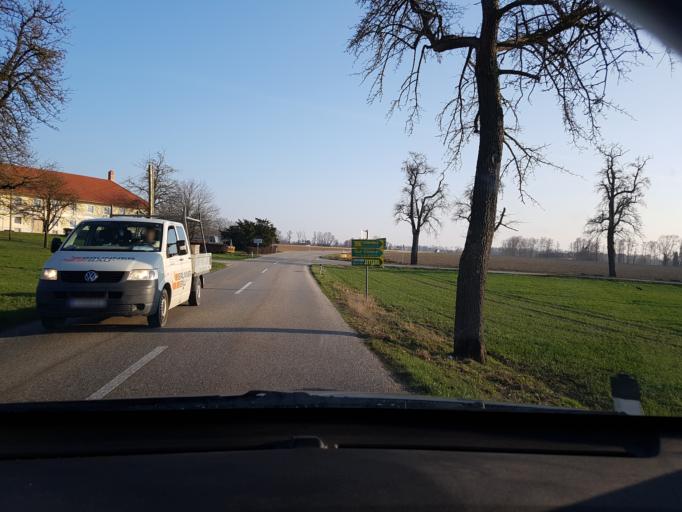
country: AT
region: Upper Austria
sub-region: Politischer Bezirk Linz-Land
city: Ansfelden
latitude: 48.1639
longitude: 14.2511
